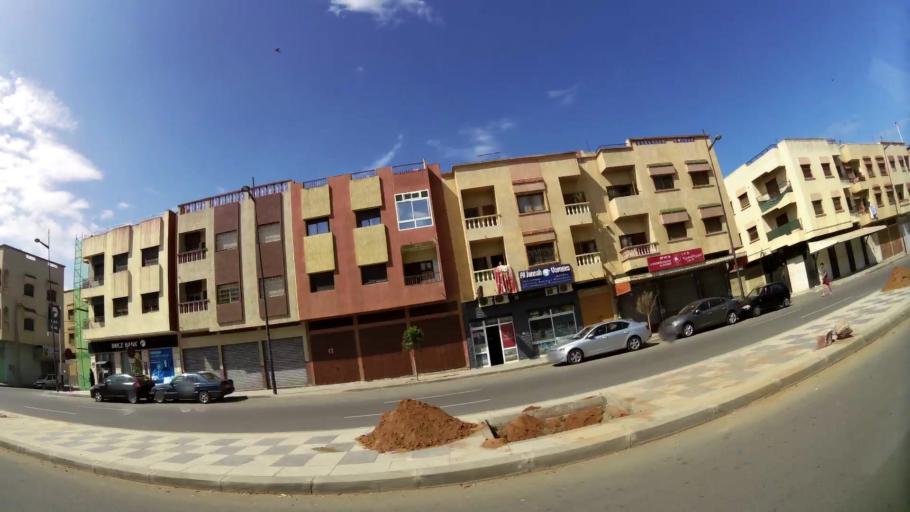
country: MA
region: Rabat-Sale-Zemmour-Zaer
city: Sale
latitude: 34.0710
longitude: -6.7945
